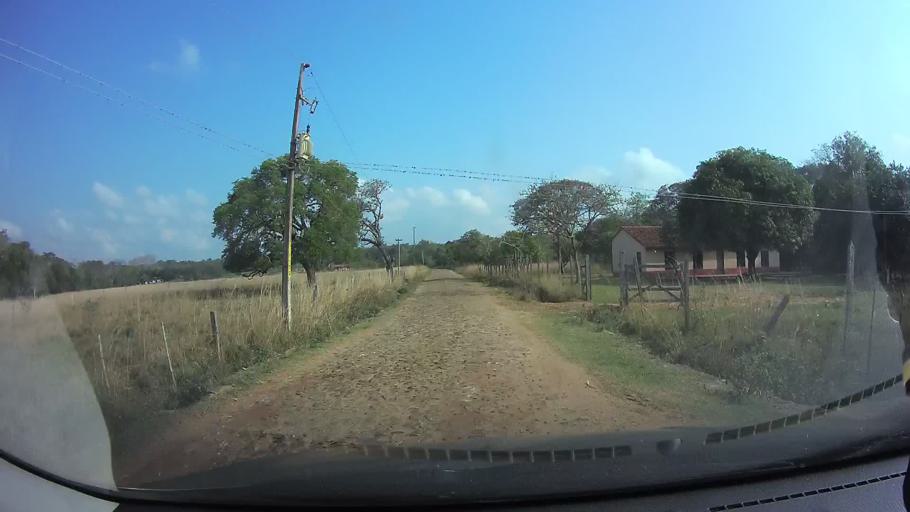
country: PY
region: Cordillera
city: Arroyos y Esteros
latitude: -25.0032
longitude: -57.1983
